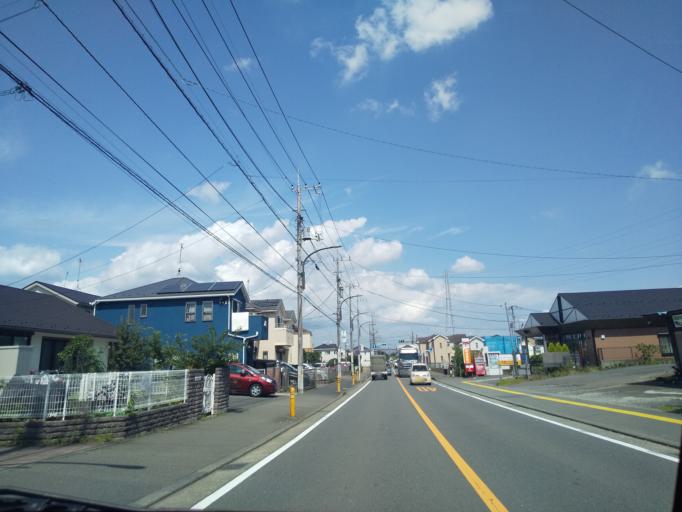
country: JP
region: Kanagawa
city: Zama
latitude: 35.4912
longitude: 139.4078
